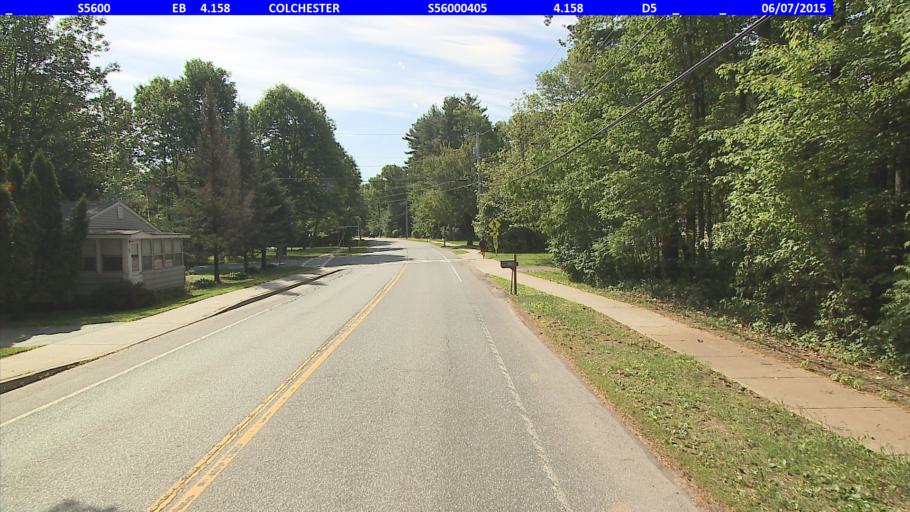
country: US
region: Vermont
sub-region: Chittenden County
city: Winooski
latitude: 44.5337
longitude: -73.2040
